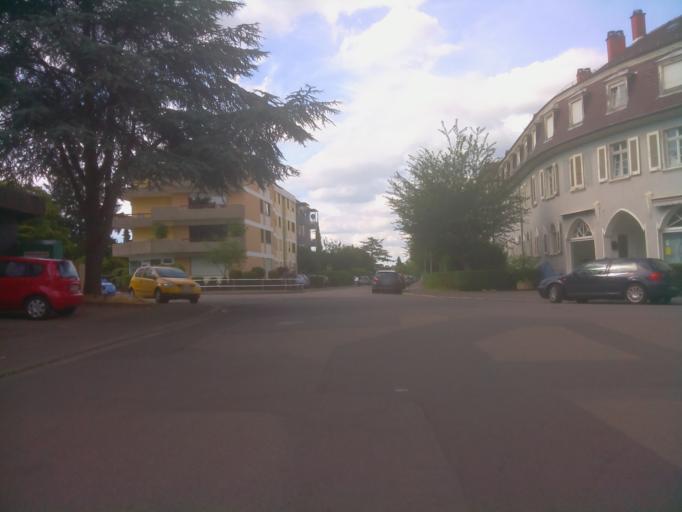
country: DE
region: Baden-Wuerttemberg
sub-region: Karlsruhe Region
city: Dossenheim
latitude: 49.4297
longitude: 8.6800
